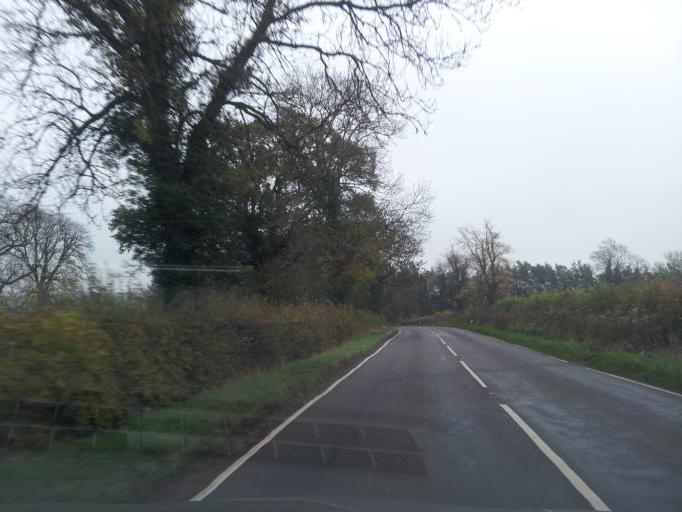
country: GB
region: England
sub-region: Buckinghamshire
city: Buckingham
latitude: 52.0190
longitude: -1.0639
